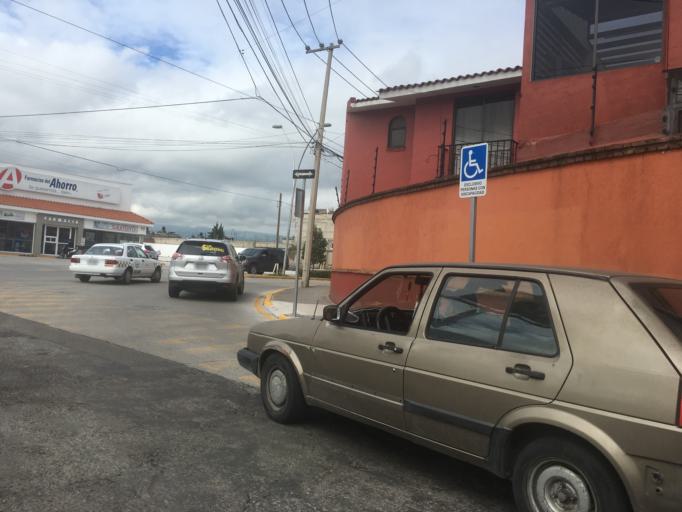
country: MX
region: Morelos
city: Metepec
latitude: 19.2621
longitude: -99.6078
